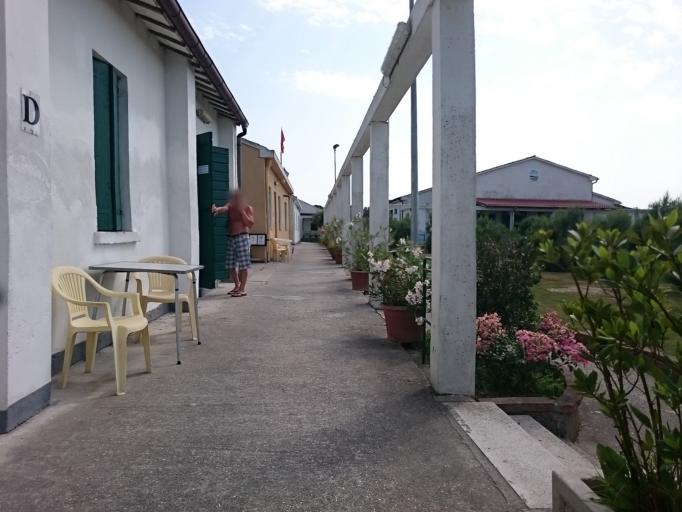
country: IT
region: Veneto
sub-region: Provincia di Venezia
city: Chioggia
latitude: 45.2423
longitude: 12.2928
